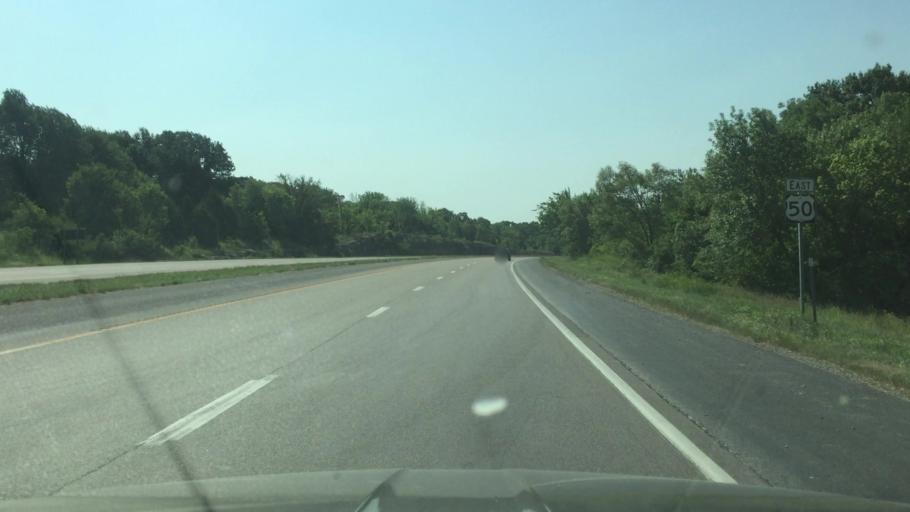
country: US
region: Missouri
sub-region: Pettis County
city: Sedalia
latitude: 38.7345
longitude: -93.3113
